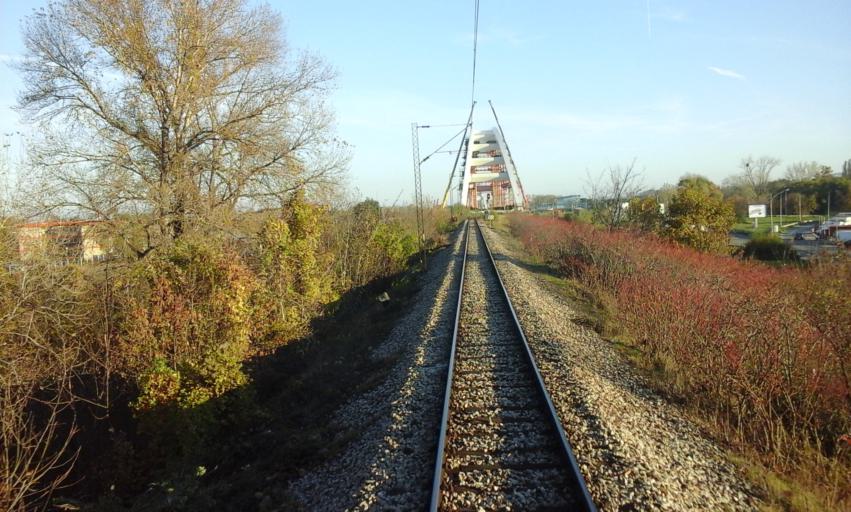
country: RS
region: Autonomna Pokrajina Vojvodina
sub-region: Juznobacki Okrug
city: Novi Sad
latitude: 45.2660
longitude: 19.8527
